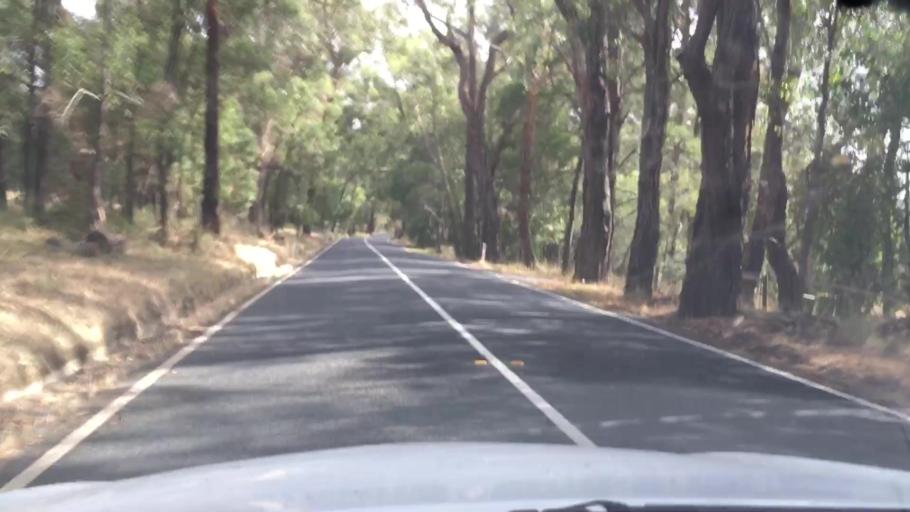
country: AU
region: Victoria
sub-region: Yarra Ranges
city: Macclesfield
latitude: -37.8406
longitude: 145.4868
